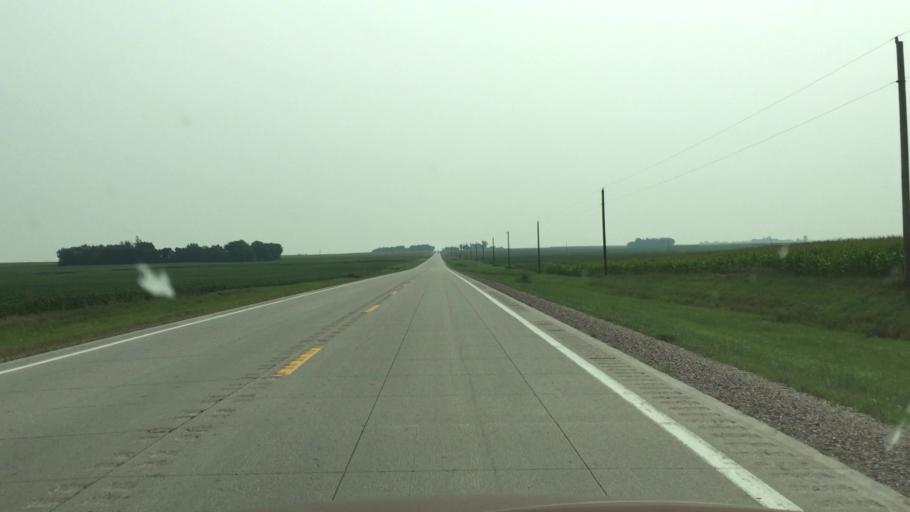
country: US
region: Iowa
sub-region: Osceola County
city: Sibley
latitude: 43.4327
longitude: -95.6900
